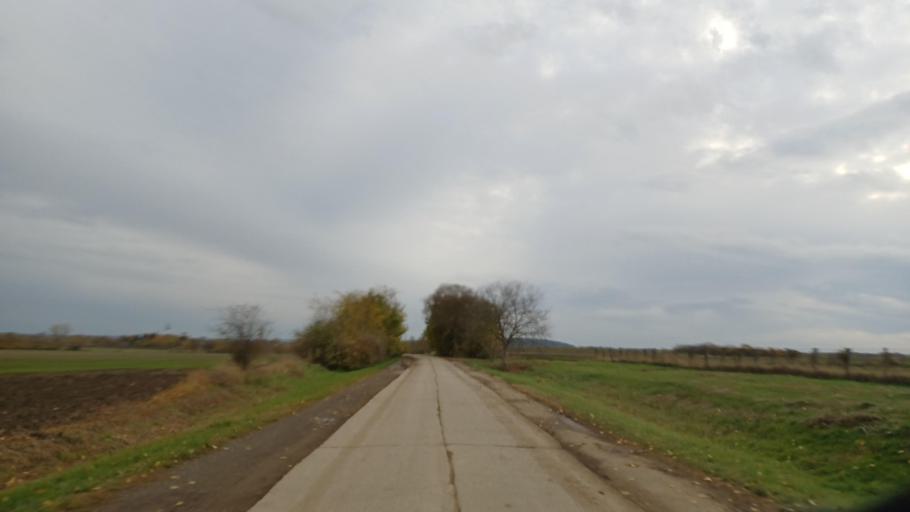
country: HU
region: Tolna
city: Nagydorog
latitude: 46.6368
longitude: 18.6052
